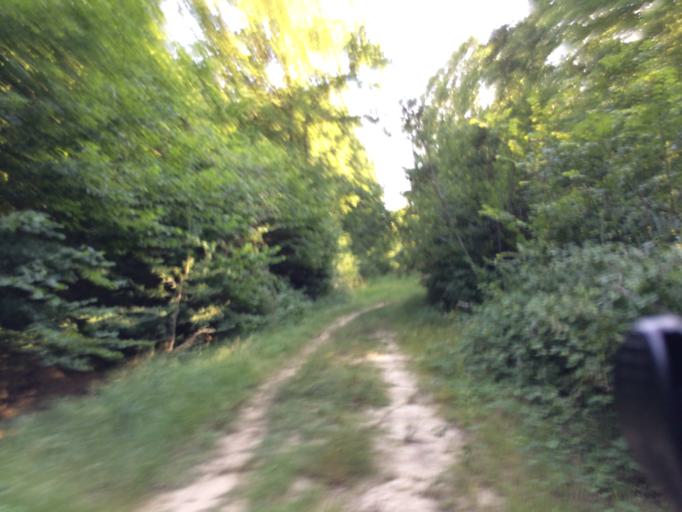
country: FR
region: Ile-de-France
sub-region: Departement de l'Essonne
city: Etiolles
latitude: 48.6478
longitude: 2.4778
